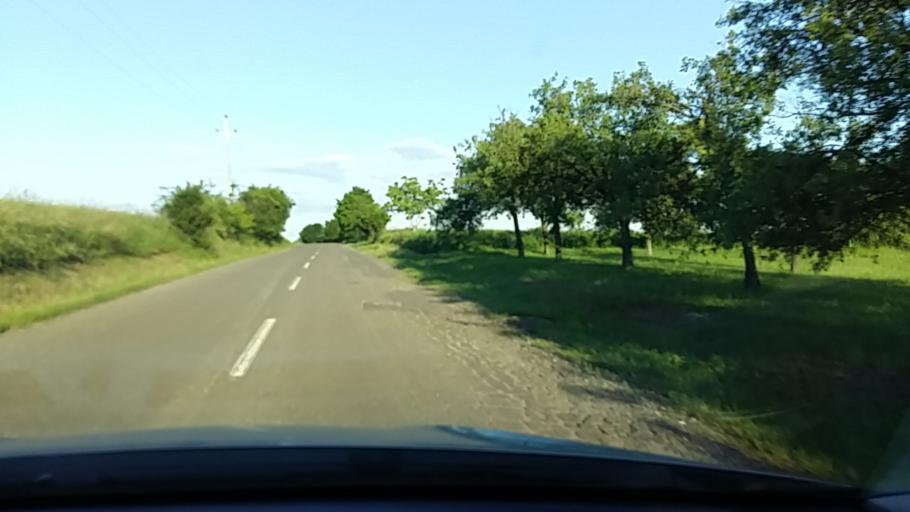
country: HU
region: Nograd
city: Diosjeno
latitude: 47.9068
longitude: 19.0591
